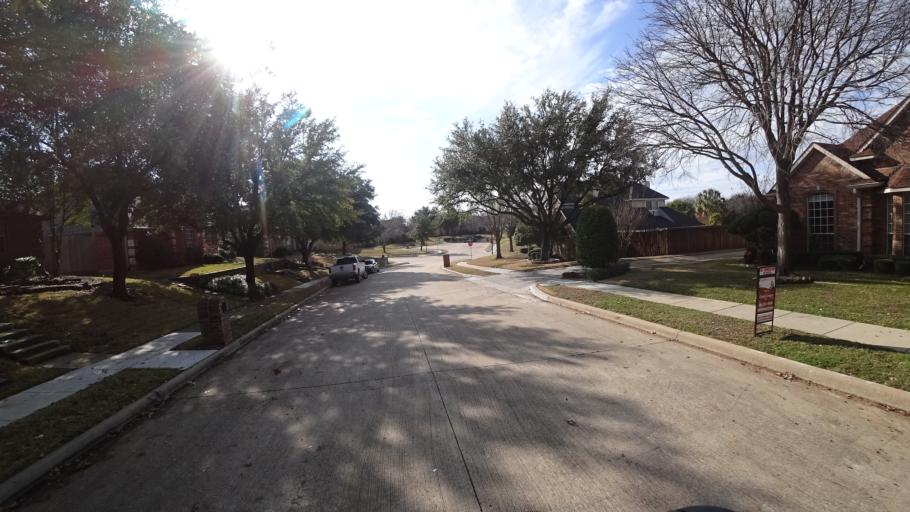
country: US
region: Texas
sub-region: Denton County
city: Lewisville
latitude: 33.0162
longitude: -97.0137
